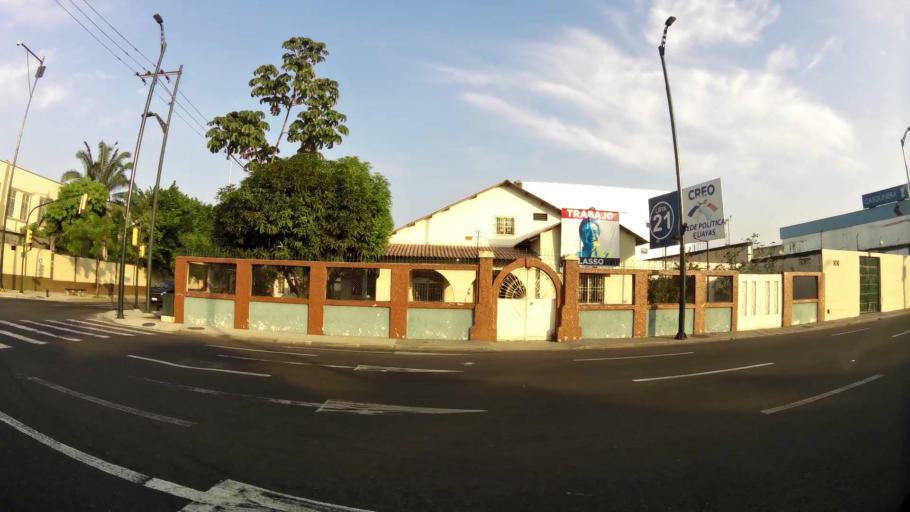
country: EC
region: Guayas
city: Guayaquil
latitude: -2.2022
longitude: -79.8932
